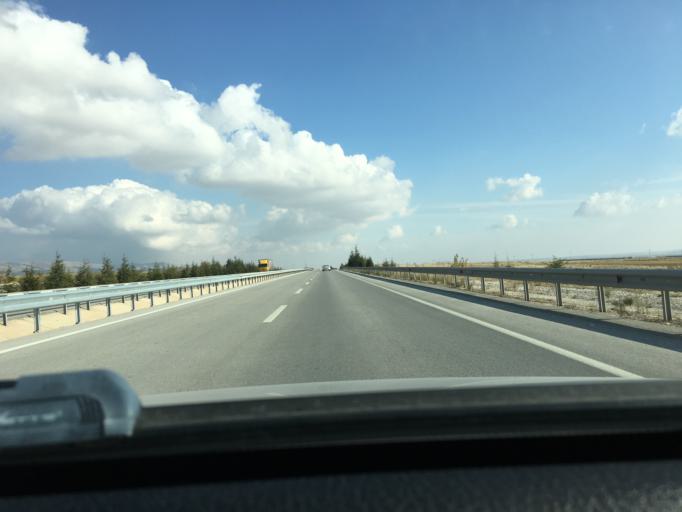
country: TR
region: Eskisehir
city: Kaymaz
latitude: 39.4861
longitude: 31.2810
